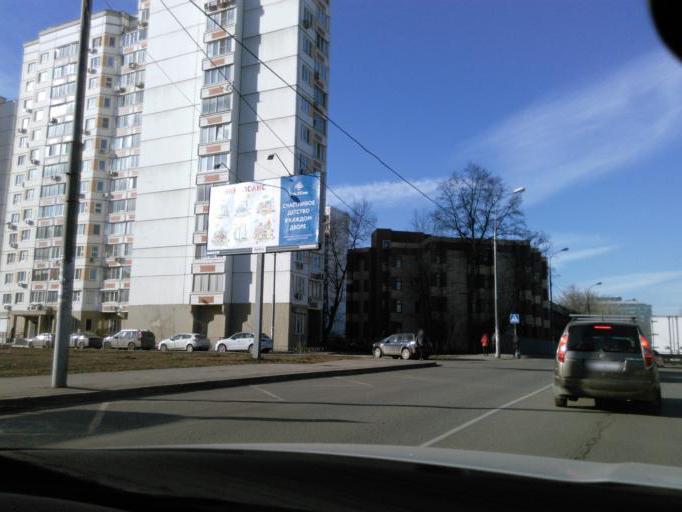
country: RU
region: Moskovskaya
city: Koptevo
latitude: 55.8248
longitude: 37.5088
